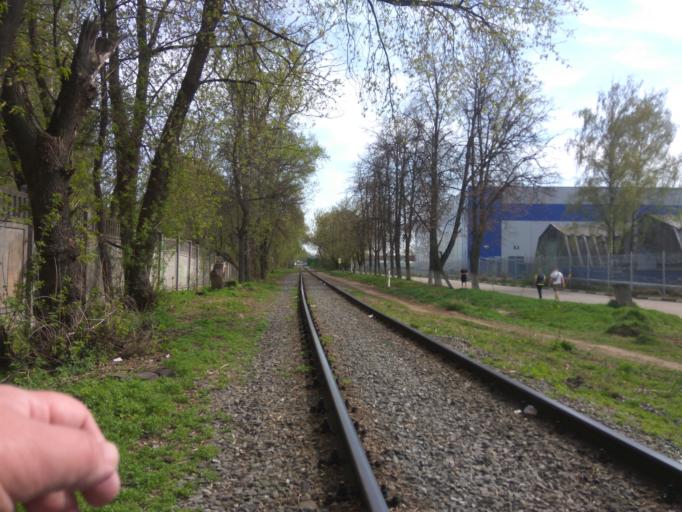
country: RU
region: Moskovskaya
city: Bykovo
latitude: 55.6276
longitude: 38.0605
